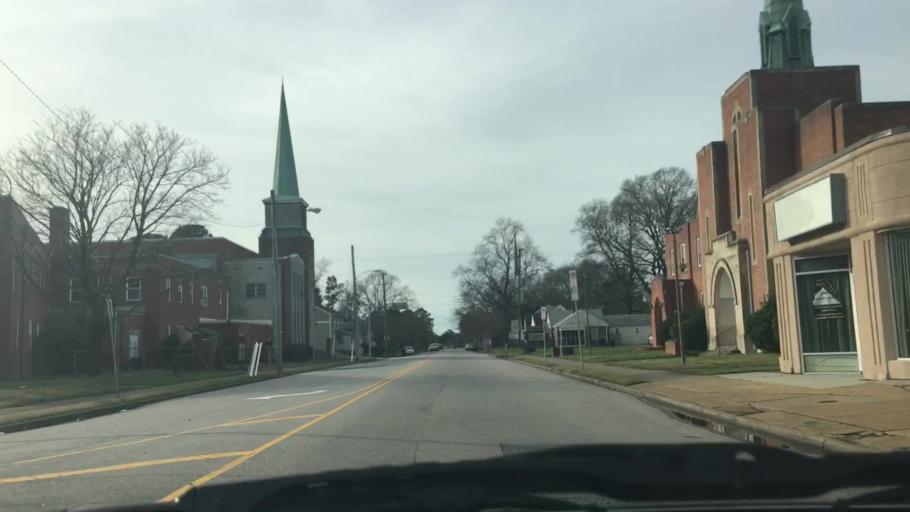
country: US
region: Virginia
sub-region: City of Norfolk
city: Norfolk
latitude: 36.8898
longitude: -76.2394
